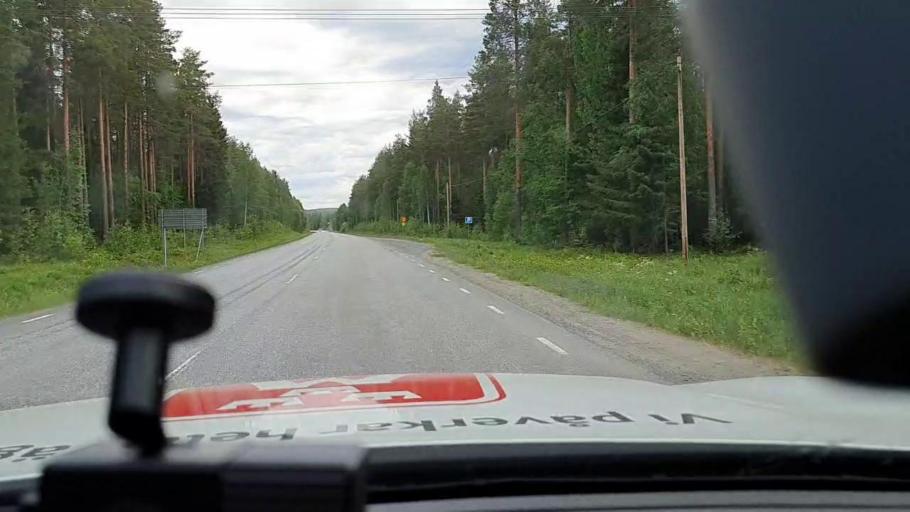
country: SE
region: Norrbotten
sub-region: Bodens Kommun
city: Boden
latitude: 65.8079
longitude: 21.6549
